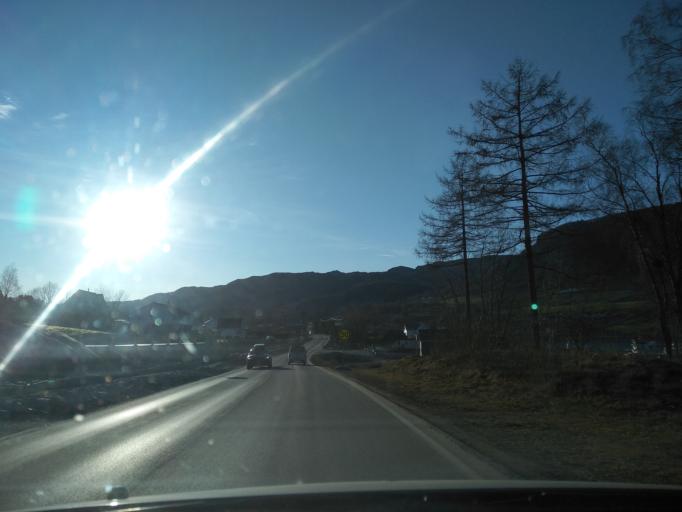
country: NO
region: Rogaland
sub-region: Vindafjord
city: Olen
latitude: 59.5991
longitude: 5.7523
